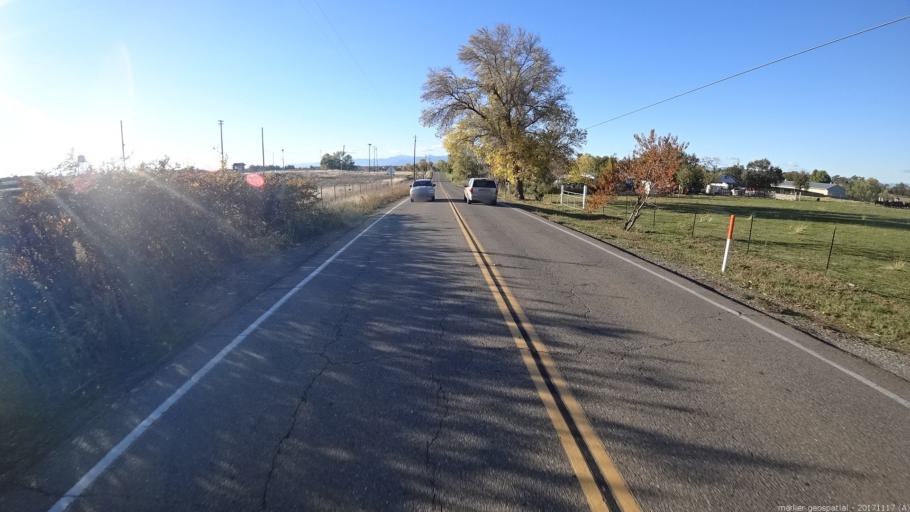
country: US
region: California
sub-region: Shasta County
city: Anderson
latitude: 40.4393
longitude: -122.2726
